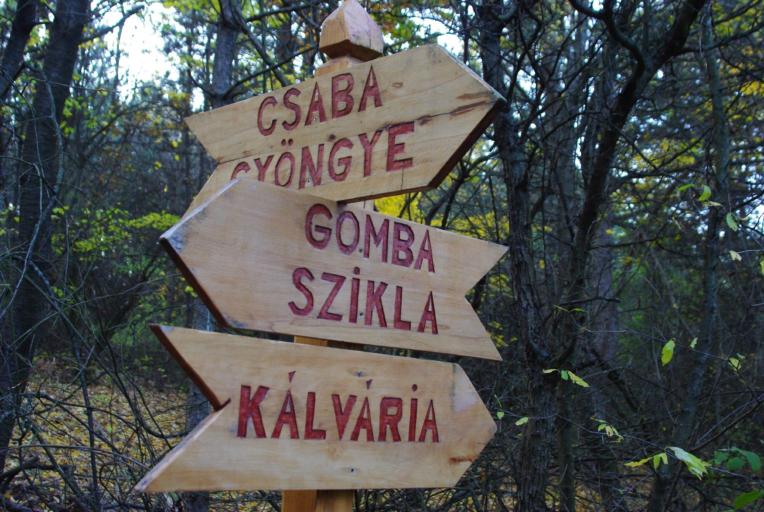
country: HU
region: Pest
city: Piliscsaba
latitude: 47.6250
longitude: 18.8372
